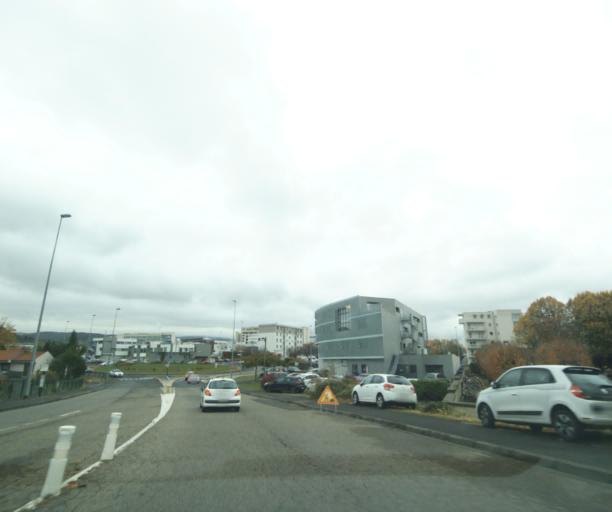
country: FR
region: Auvergne
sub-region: Departement du Puy-de-Dome
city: Beaumont
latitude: 45.7559
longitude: 3.0963
